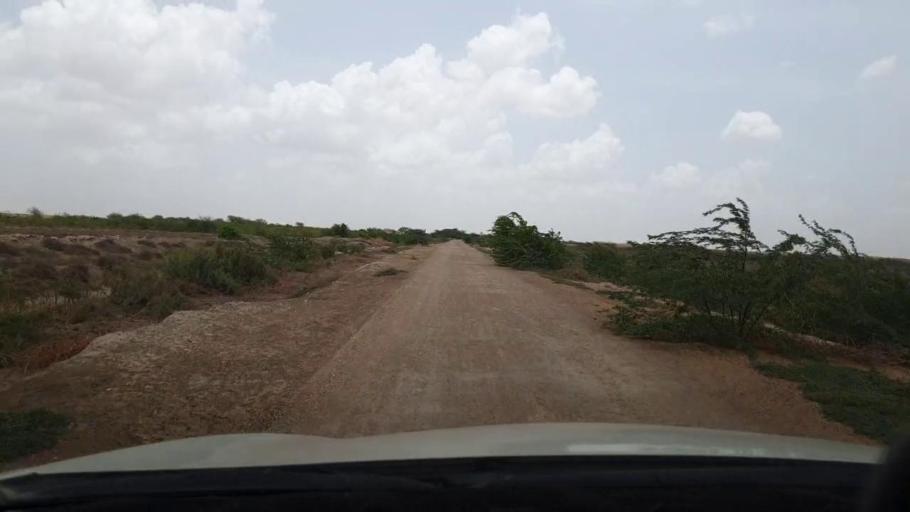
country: PK
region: Sindh
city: Kadhan
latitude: 24.3513
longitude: 68.9234
